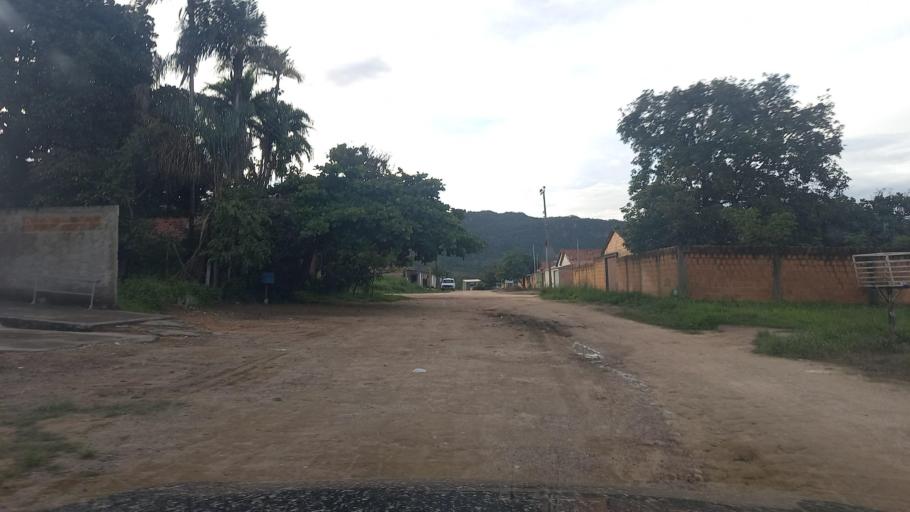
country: BR
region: Goias
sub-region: Cavalcante
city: Cavalcante
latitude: -13.7886
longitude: -47.4580
